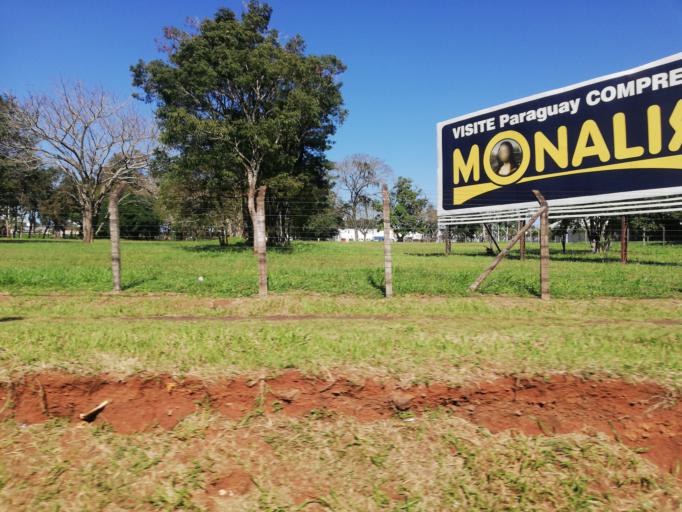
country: BR
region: Parana
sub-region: Foz Do Iguacu
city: Foz do Iguacu
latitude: -25.5551
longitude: -54.5665
